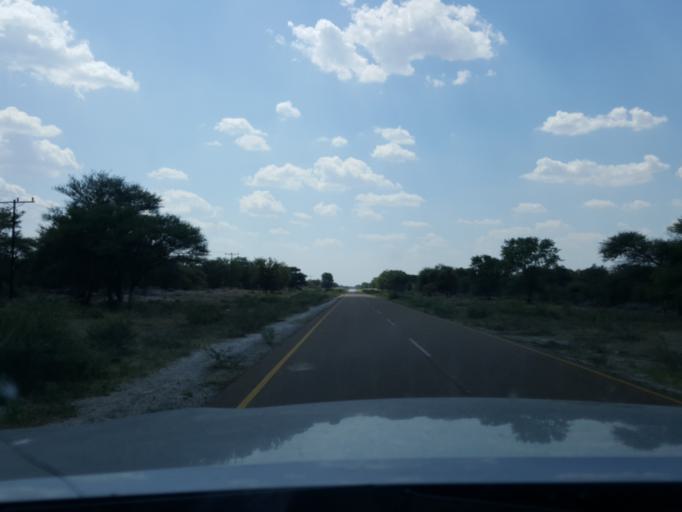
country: BW
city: Nokaneng
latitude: -19.7436
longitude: 22.1974
